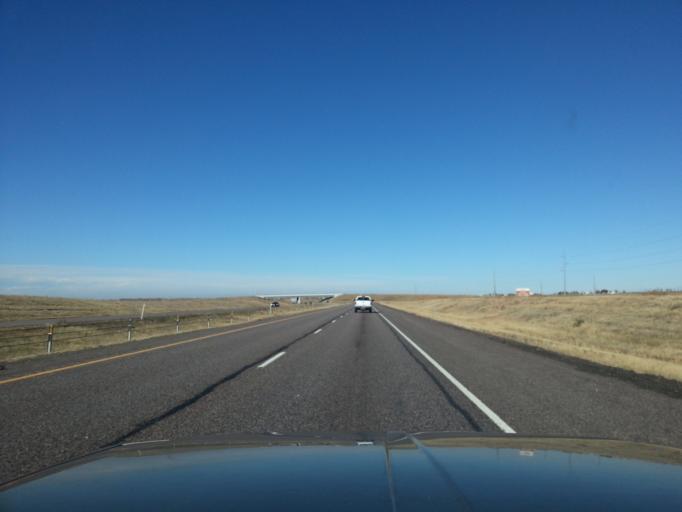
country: US
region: Colorado
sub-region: Adams County
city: Brighton
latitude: 39.8943
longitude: -104.7617
